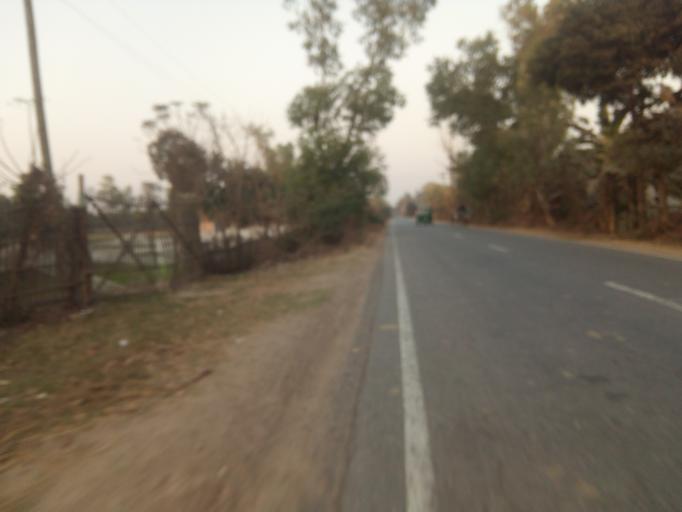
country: BD
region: Rajshahi
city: Bogra
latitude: 24.6381
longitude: 89.2503
